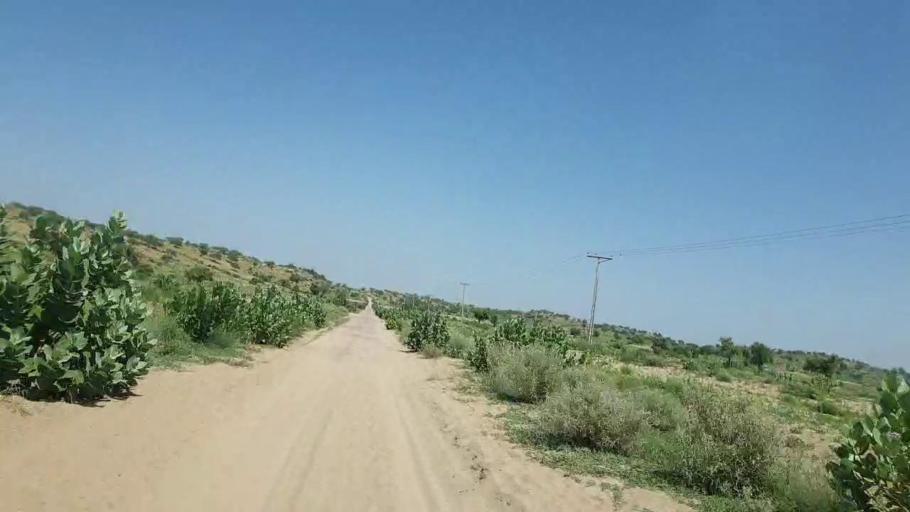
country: PK
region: Sindh
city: Islamkot
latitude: 25.1677
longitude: 70.4164
